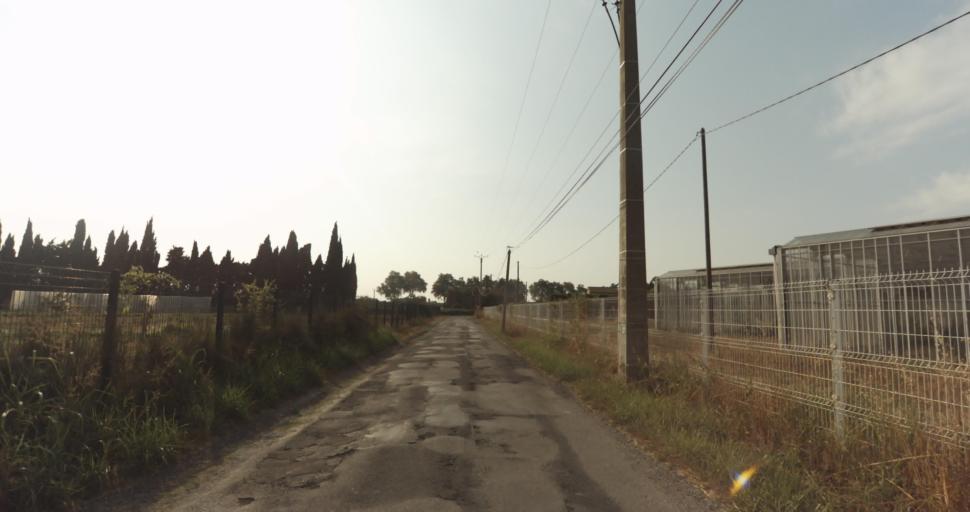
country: FR
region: Languedoc-Roussillon
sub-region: Departement des Pyrenees-Orientales
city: Alenya
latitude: 42.6222
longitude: 2.9748
